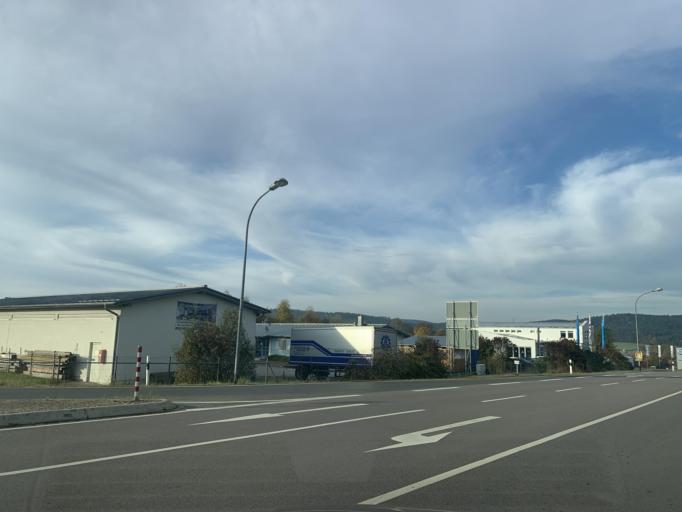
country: DE
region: Bavaria
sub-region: Upper Palatinate
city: Neunburg vorm Wald
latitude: 49.3385
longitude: 12.3925
